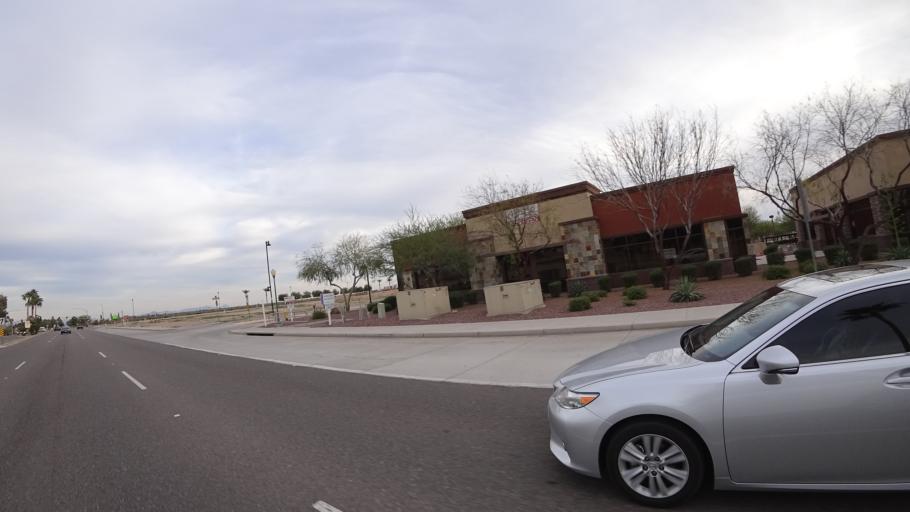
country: US
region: Arizona
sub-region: Maricopa County
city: Sun City West
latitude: 33.6386
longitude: -112.3796
